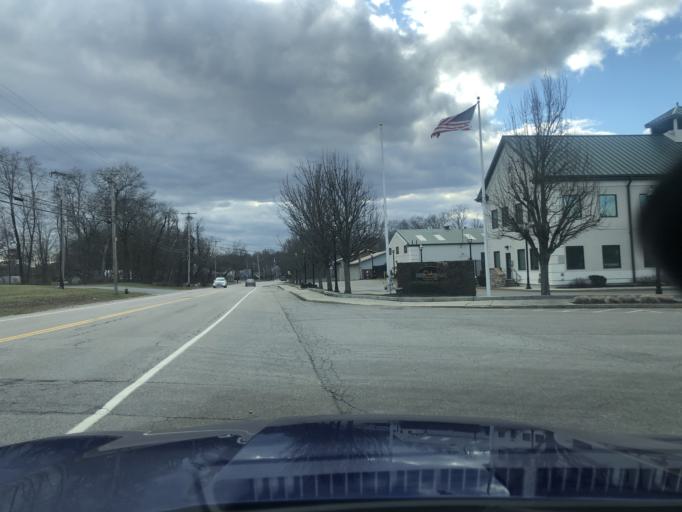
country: US
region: Massachusetts
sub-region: Norfolk County
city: Avon
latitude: 42.1159
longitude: -71.0210
